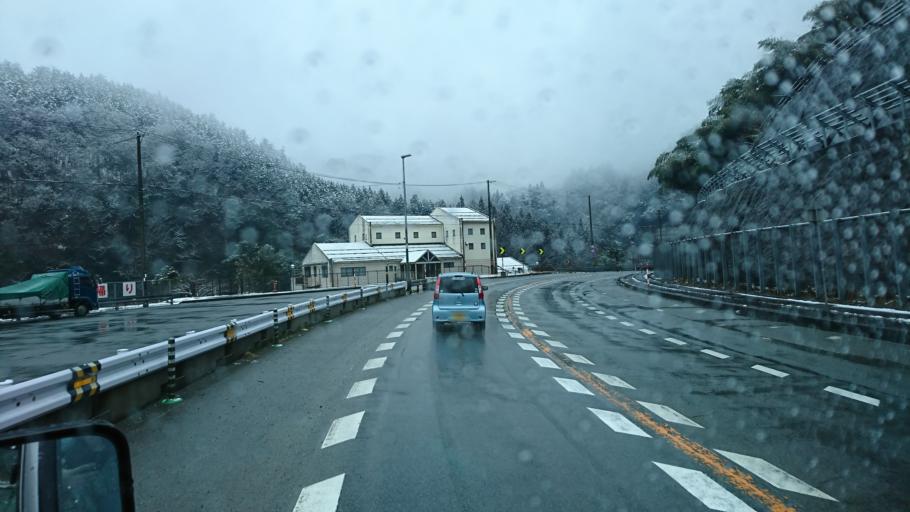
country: JP
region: Hyogo
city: Toyooka
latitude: 35.4778
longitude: 134.5852
